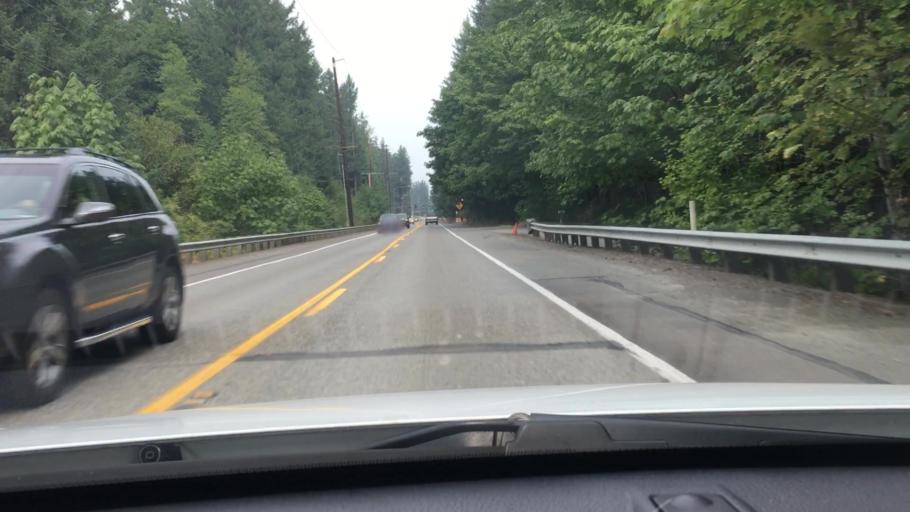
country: US
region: Washington
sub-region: King County
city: Ravensdale
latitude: 47.3475
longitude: -122.0189
